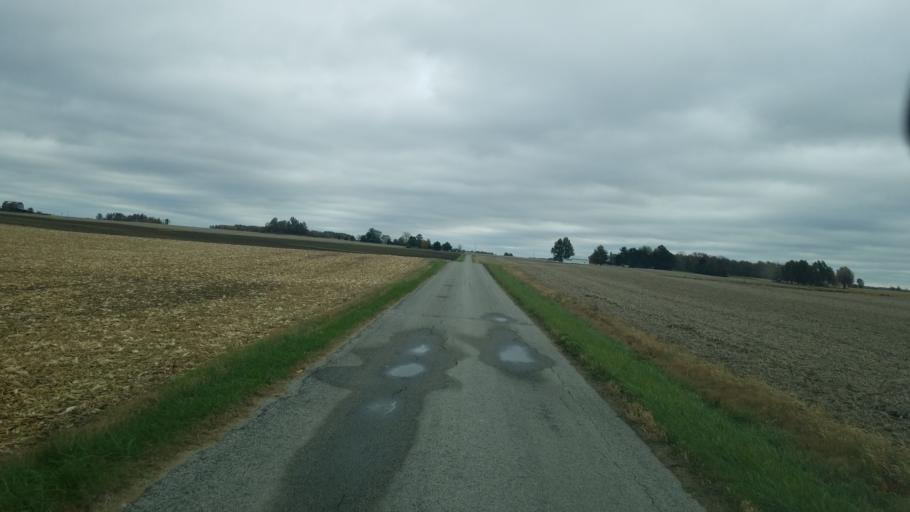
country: US
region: Ohio
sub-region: Crawford County
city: Bucyrus
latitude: 40.9073
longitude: -82.8626
